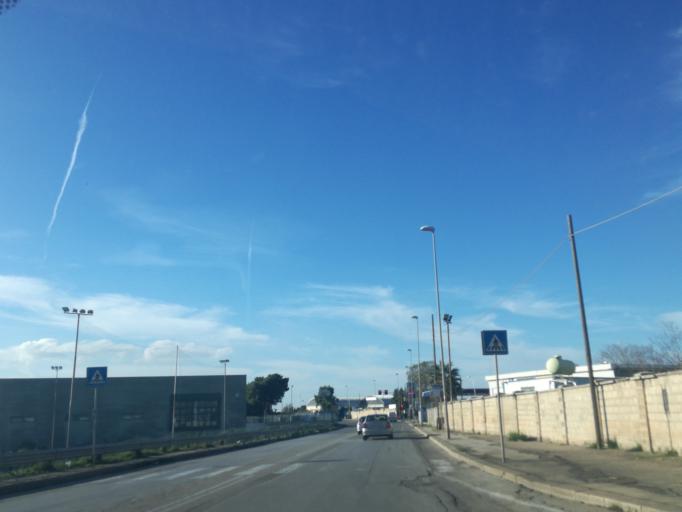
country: IT
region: Apulia
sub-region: Provincia di Bari
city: Bari
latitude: 41.1225
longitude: 16.8349
